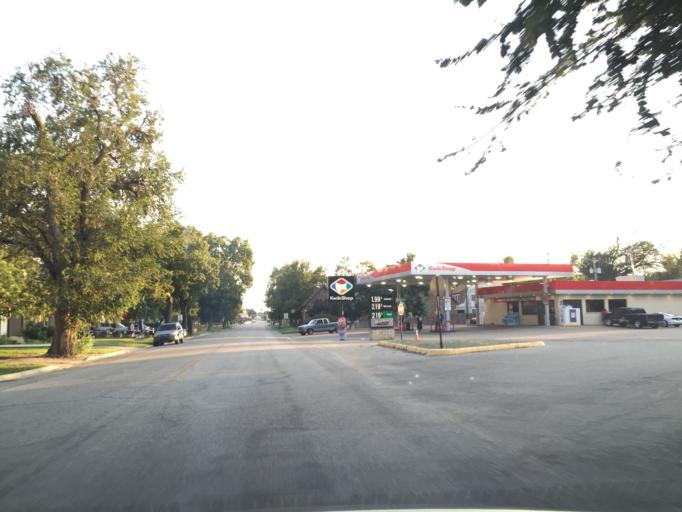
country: US
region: Kansas
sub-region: Ellsworth County
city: Ellsworth
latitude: 38.7330
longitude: -98.2272
